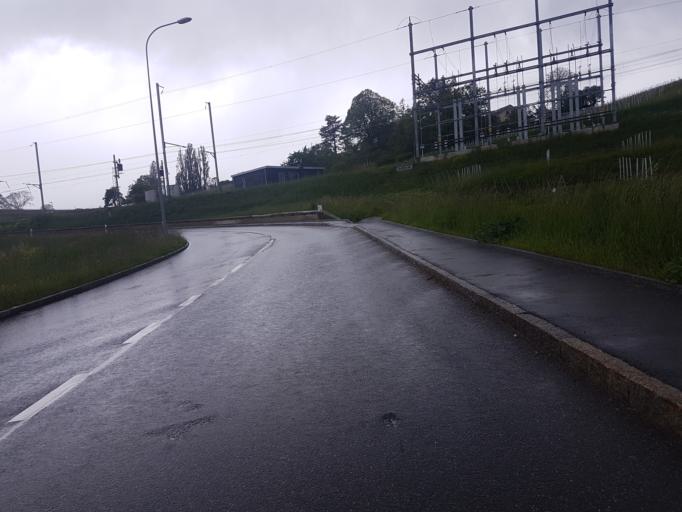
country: CH
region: Geneva
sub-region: Geneva
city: Aire-la-Ville
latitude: 46.1932
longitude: 6.0242
